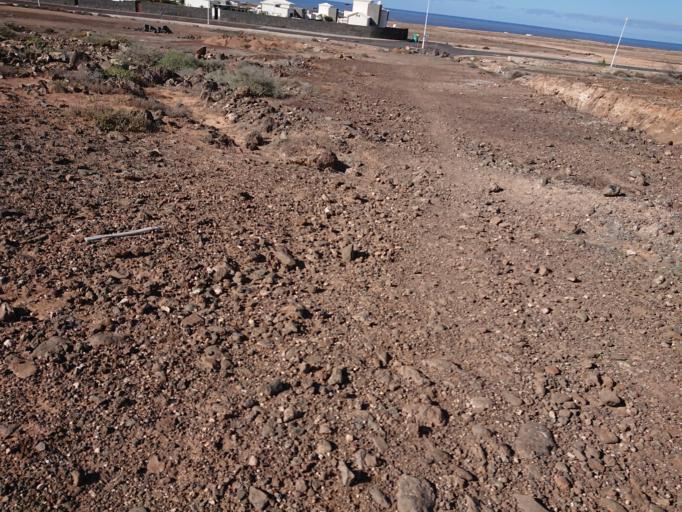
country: ES
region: Canary Islands
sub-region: Provincia de Las Palmas
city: Playa Blanca
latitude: 28.8719
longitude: -13.8625
